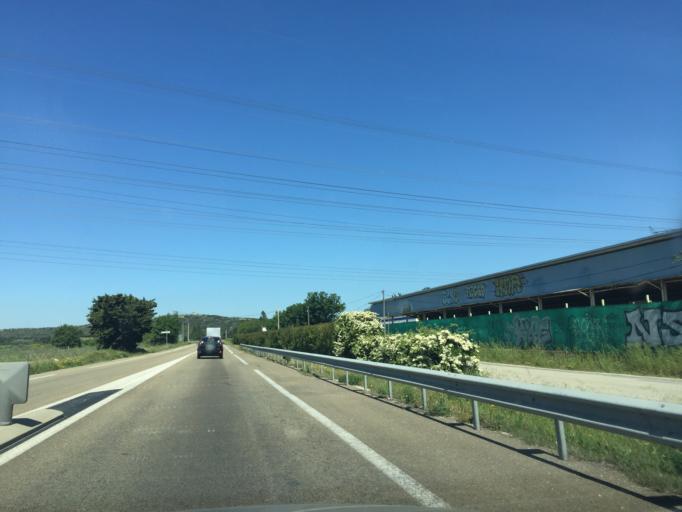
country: FR
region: Languedoc-Roussillon
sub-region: Departement du Gard
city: Saze
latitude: 43.9526
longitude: 4.6647
